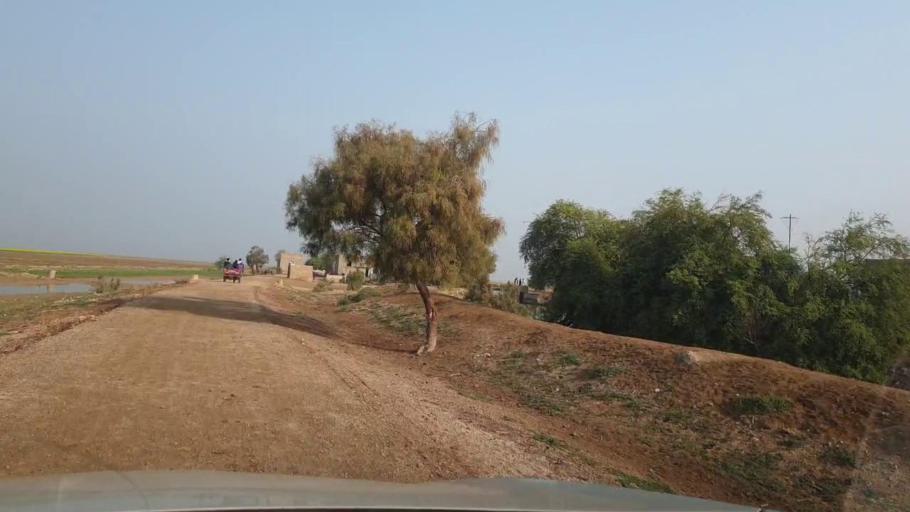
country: PK
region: Sindh
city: Sehwan
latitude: 26.3520
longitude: 67.7232
